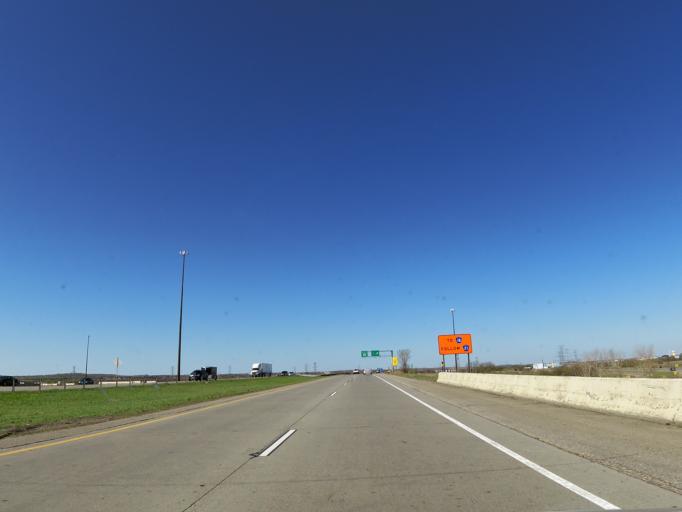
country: US
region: Minnesota
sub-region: Scott County
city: Prior Lake
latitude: 44.7871
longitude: -93.4107
